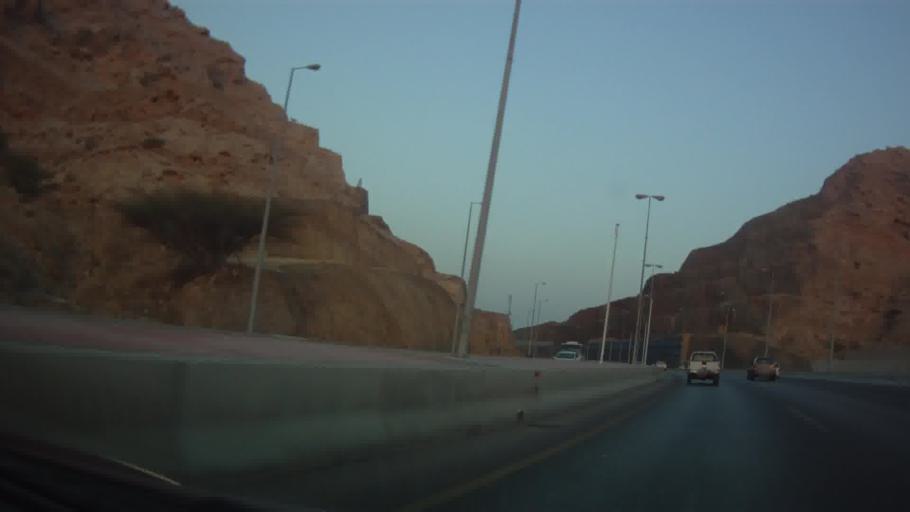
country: OM
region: Muhafazat Masqat
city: Muscat
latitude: 23.6153
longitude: 58.5279
